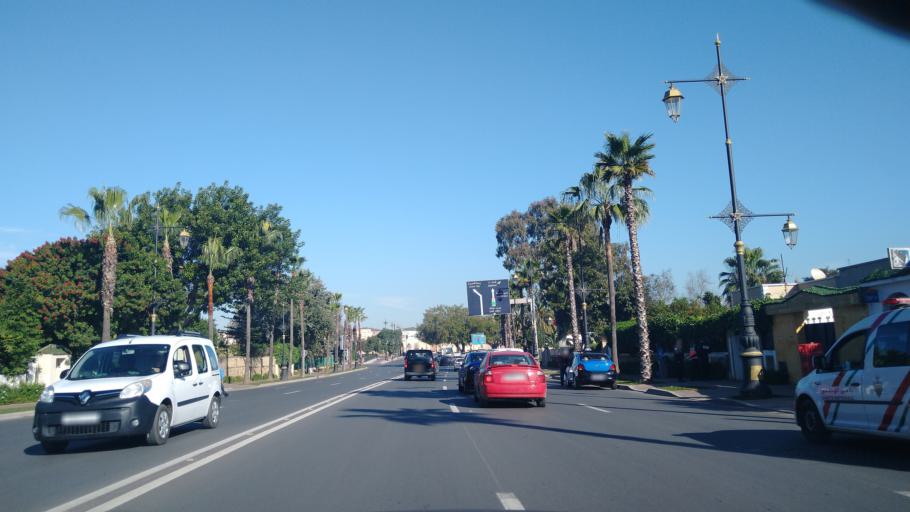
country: MA
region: Rabat-Sale-Zemmour-Zaer
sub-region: Rabat
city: Rabat
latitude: 34.0036
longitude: -6.8271
